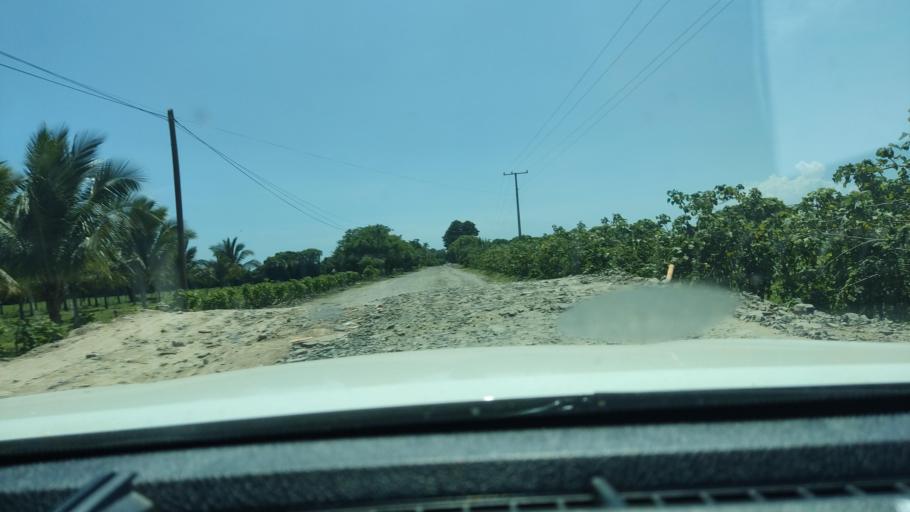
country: SV
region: Ahuachapan
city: San Francisco Menendez
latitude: 13.7538
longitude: -90.1283
